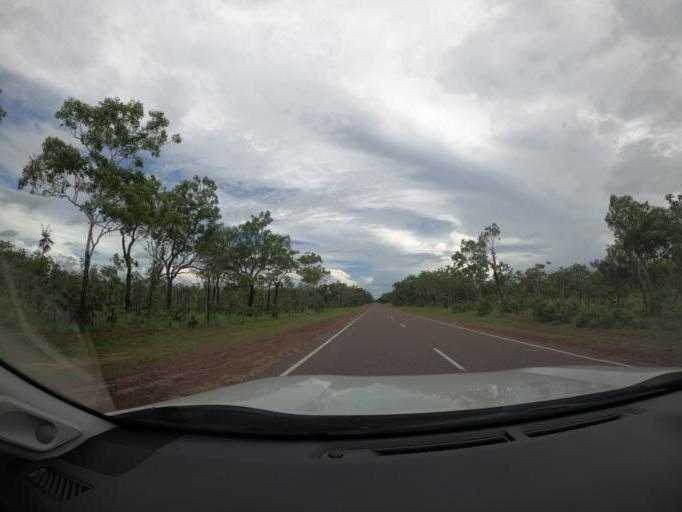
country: AU
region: Northern Territory
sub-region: Litchfield
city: McMinns Lagoon
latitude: -12.8309
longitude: 131.8852
